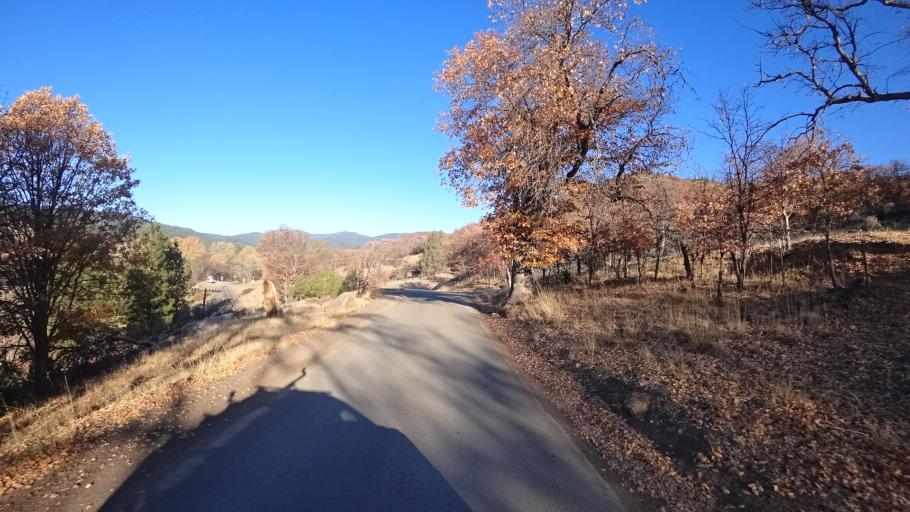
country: US
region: Oregon
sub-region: Jackson County
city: Ashland
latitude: 42.0038
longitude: -122.6427
